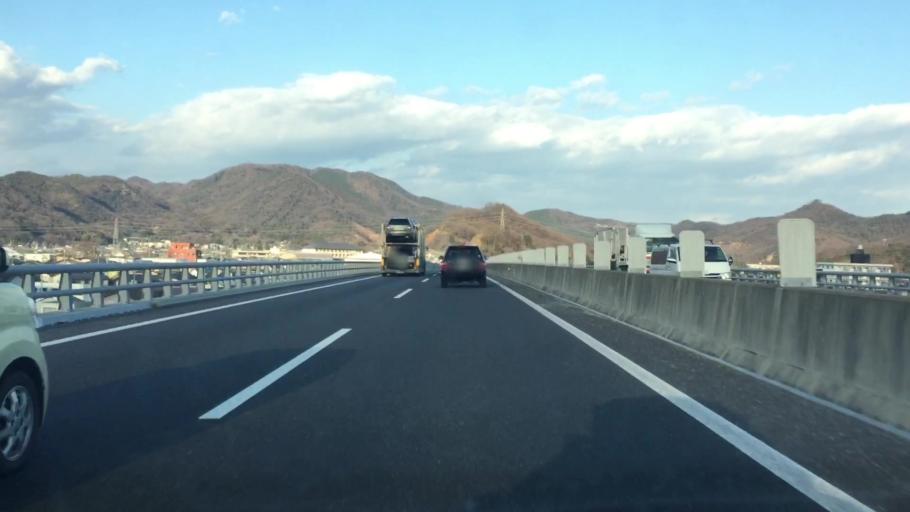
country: JP
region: Tochigi
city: Ashikaga
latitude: 36.3404
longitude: 139.4104
